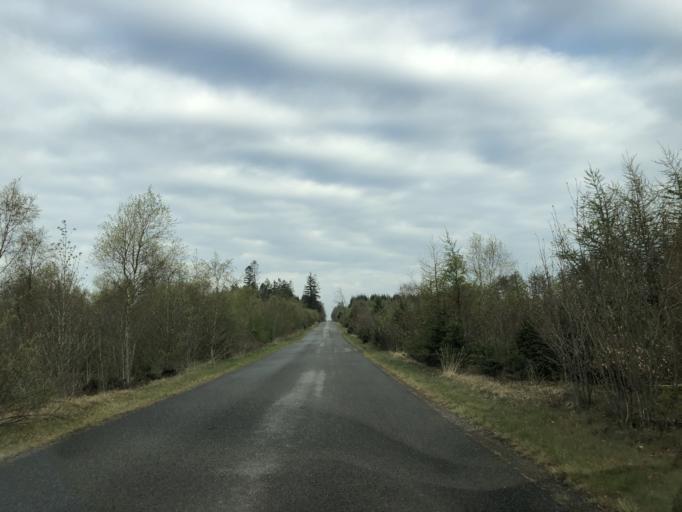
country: DK
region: Central Jutland
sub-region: Holstebro Kommune
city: Holstebro
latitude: 56.3166
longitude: 8.5200
